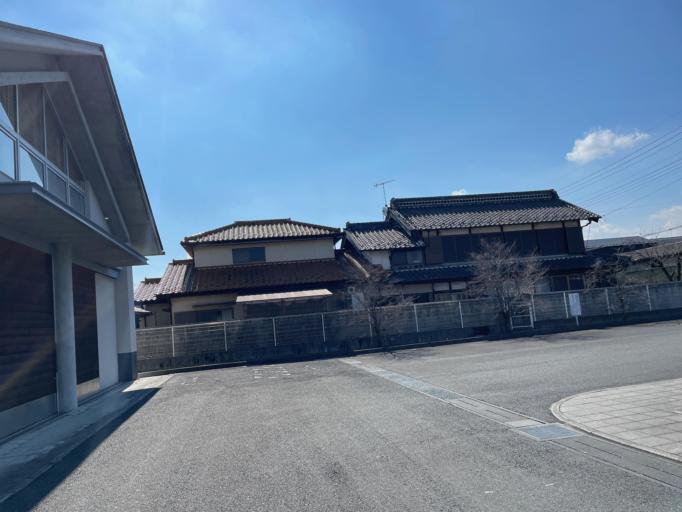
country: JP
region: Saitama
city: Yorii
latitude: 36.1158
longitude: 139.2070
